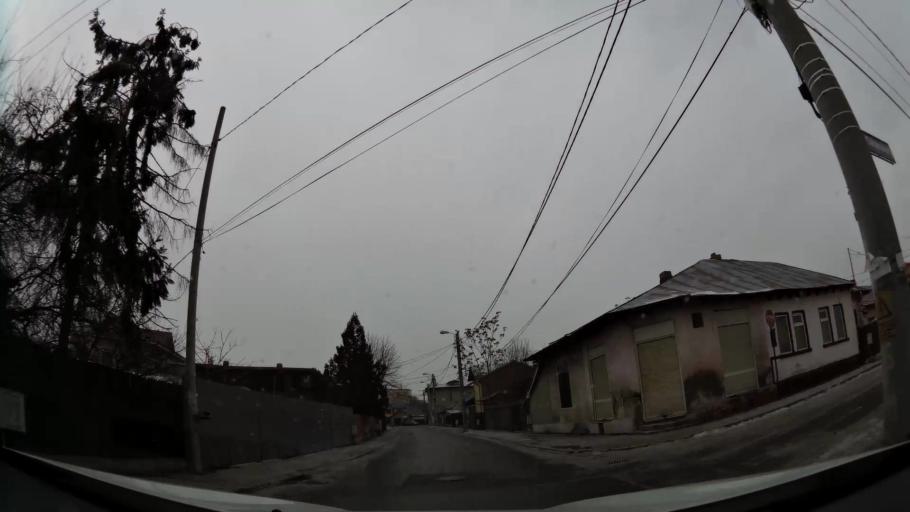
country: RO
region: Prahova
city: Ploiesti
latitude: 44.9421
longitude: 26.0459
